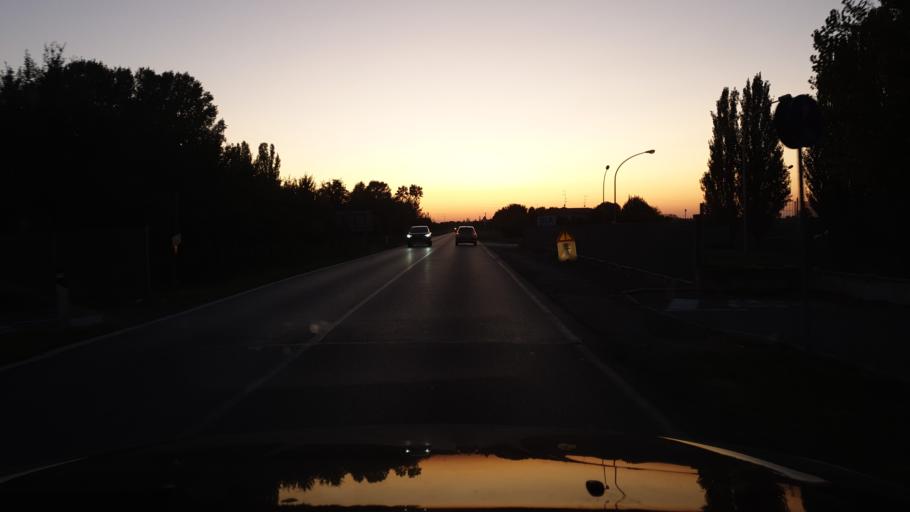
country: IT
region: Emilia-Romagna
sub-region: Provincia di Bologna
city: Altedo
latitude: 44.6827
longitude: 11.4965
